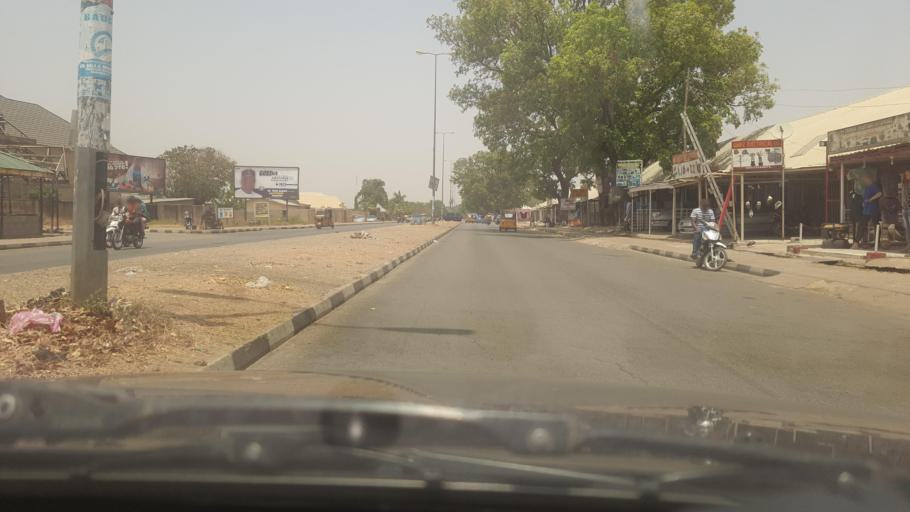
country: NG
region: Bauchi
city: Bauchi
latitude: 10.3167
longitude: 9.8285
